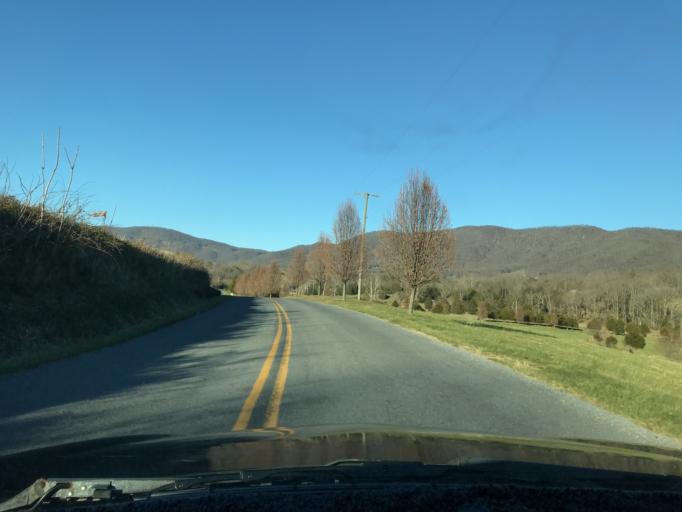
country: US
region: Virginia
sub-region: Botetourt County
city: Buchanan
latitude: 37.4359
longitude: -79.6747
